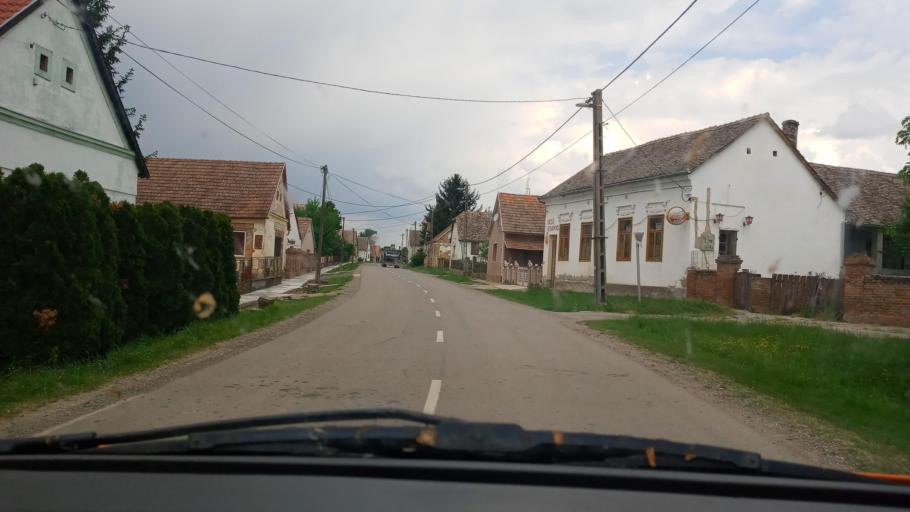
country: HU
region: Baranya
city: Villany
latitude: 45.8458
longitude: 18.4866
